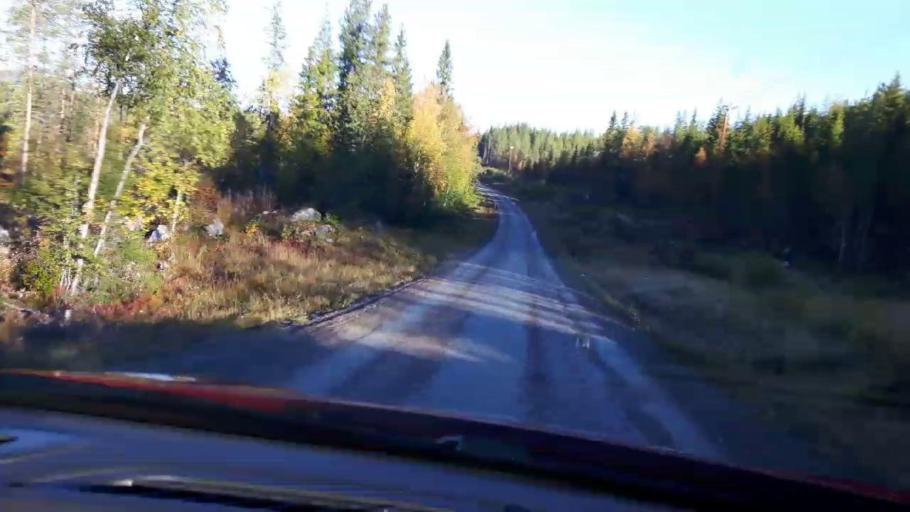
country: SE
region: Jaemtland
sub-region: Stroemsunds Kommun
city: Stroemsund
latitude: 64.3710
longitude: 15.1566
